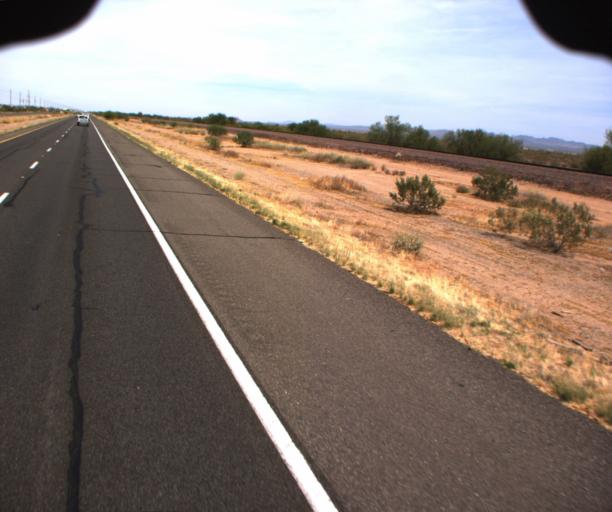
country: US
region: Arizona
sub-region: Maricopa County
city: Sun City West
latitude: 33.7206
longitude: -112.4549
